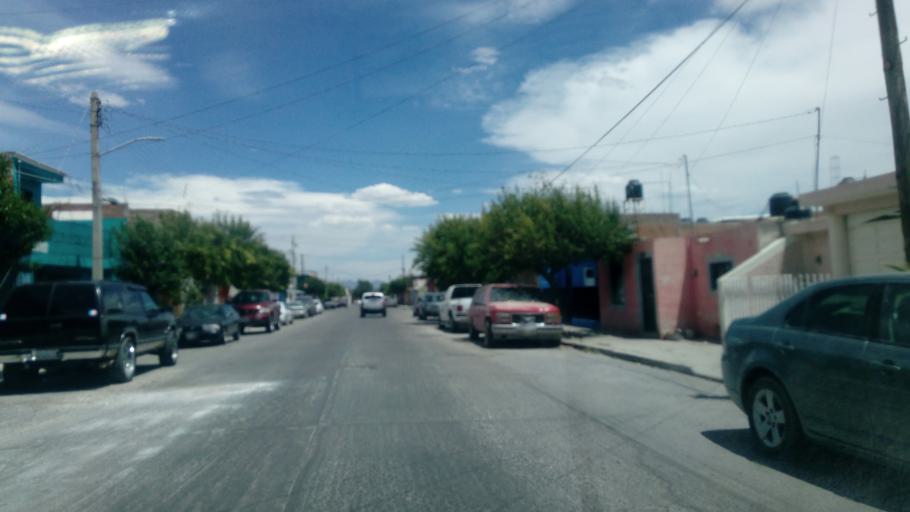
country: MX
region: Durango
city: Victoria de Durango
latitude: 24.0006
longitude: -104.6769
